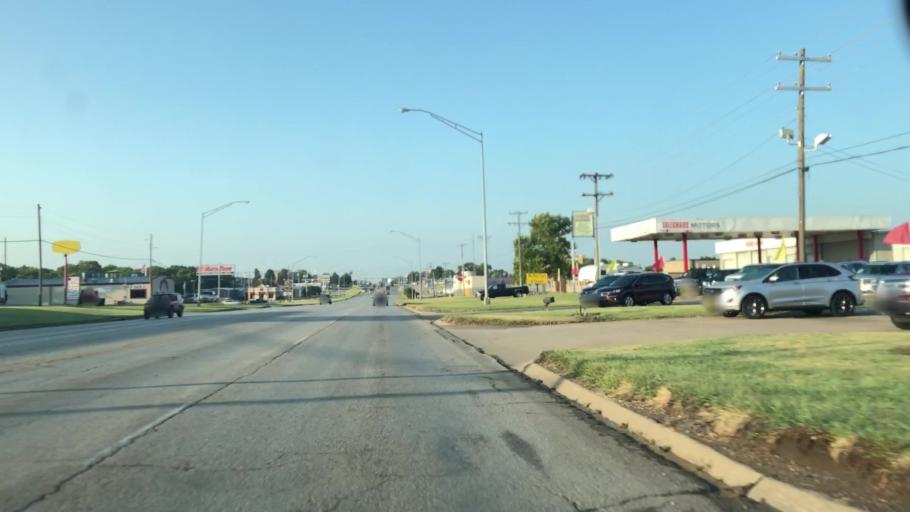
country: US
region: Oklahoma
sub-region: Washington County
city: Dewey
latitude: 36.7624
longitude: -95.9356
